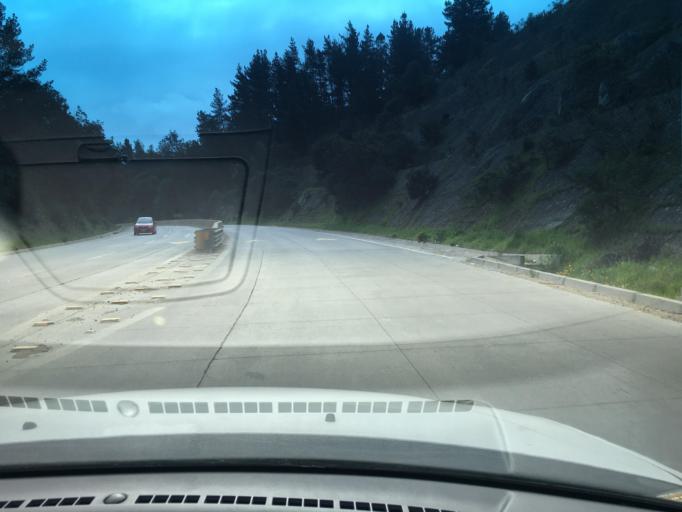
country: CL
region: Valparaiso
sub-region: Provincia de Valparaiso
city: Vina del Mar
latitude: -33.1067
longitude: -71.5570
